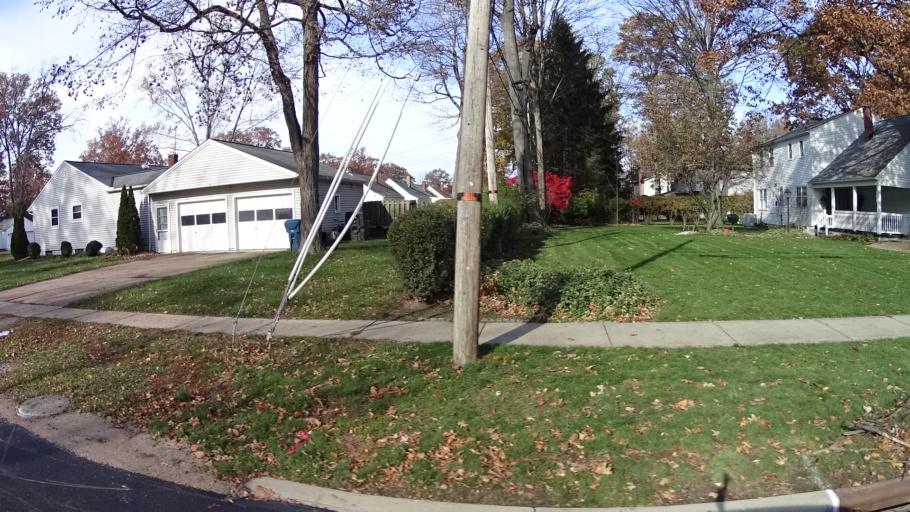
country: US
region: Ohio
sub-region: Lorain County
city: Avon Lake
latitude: 41.5026
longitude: -82.0229
